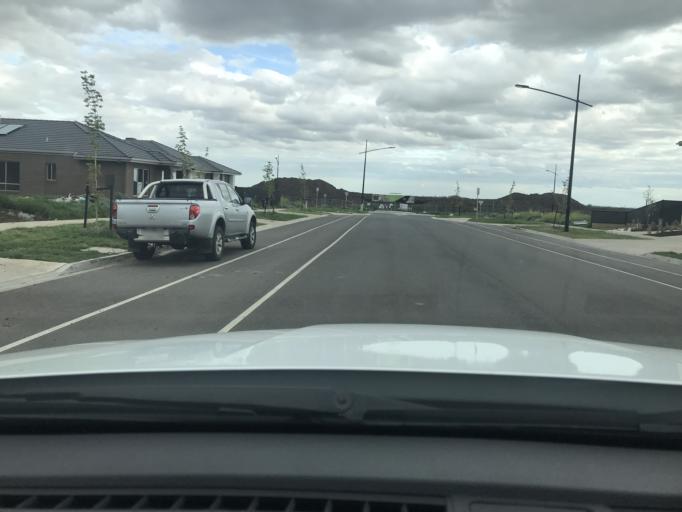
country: AU
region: Victoria
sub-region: Hume
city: Roxburgh Park
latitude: -37.6016
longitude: 144.8927
